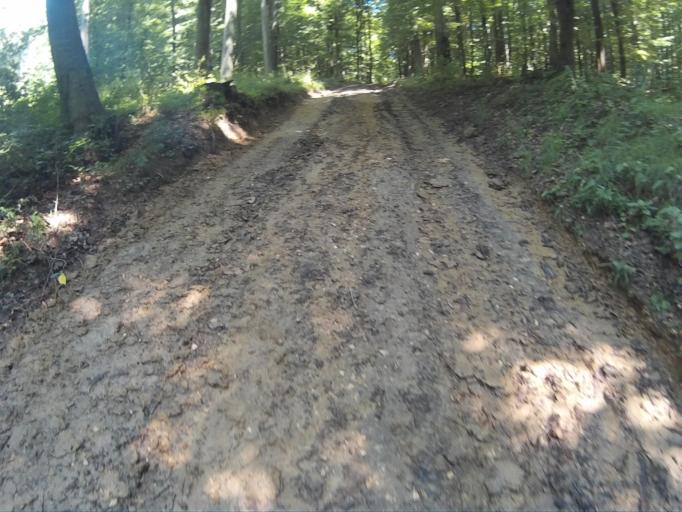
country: HU
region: Veszprem
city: Zirc
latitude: 47.1871
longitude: 17.8753
